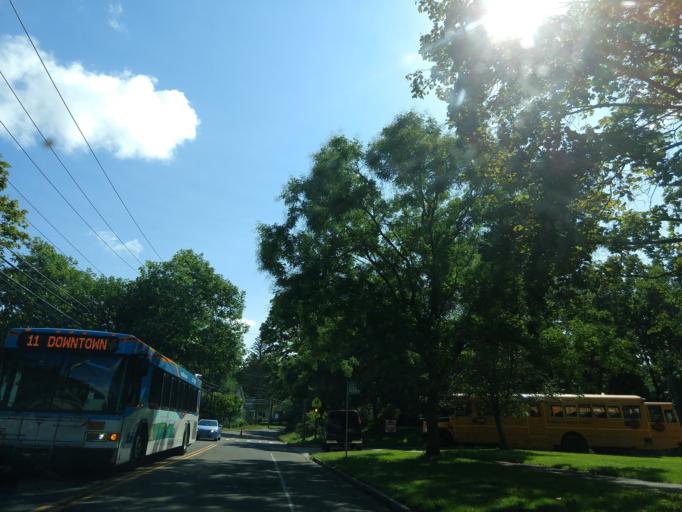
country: US
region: New York
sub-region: Tompkins County
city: South Hill
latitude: 42.4341
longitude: -76.4919
